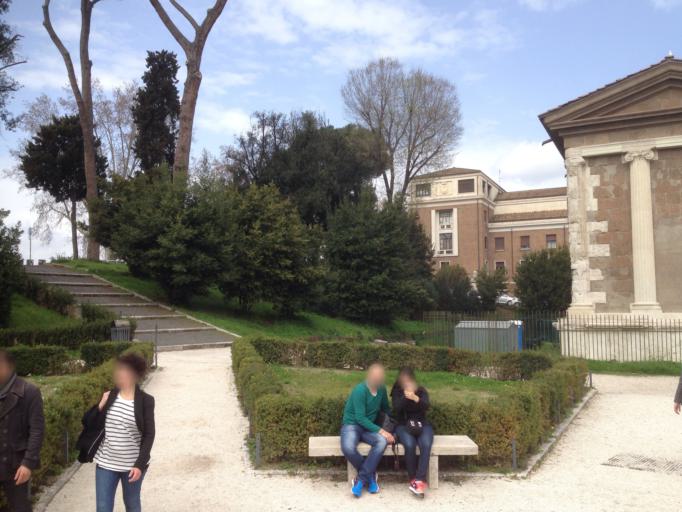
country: IT
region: Latium
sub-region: Citta metropolitana di Roma Capitale
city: Rome
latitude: 41.8889
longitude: 12.4810
